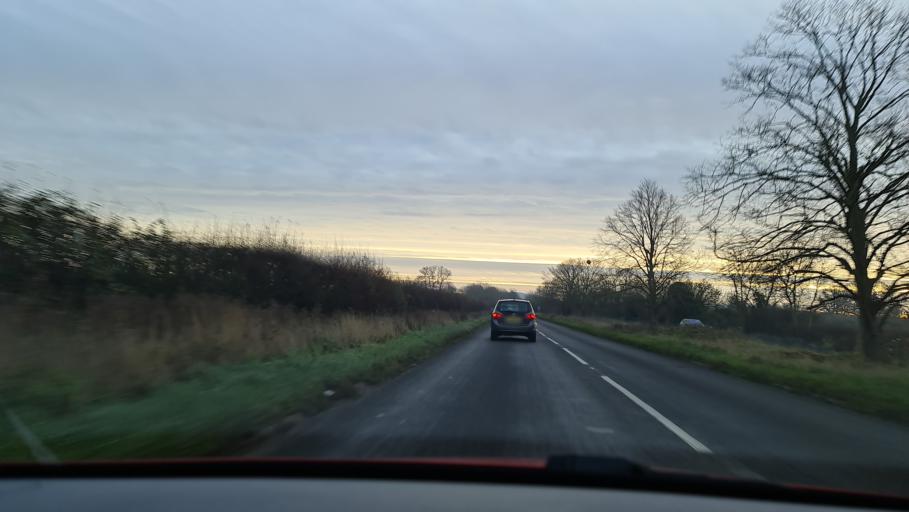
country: GB
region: England
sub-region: Buckinghamshire
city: Haddenham
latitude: 51.7530
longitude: -0.8934
